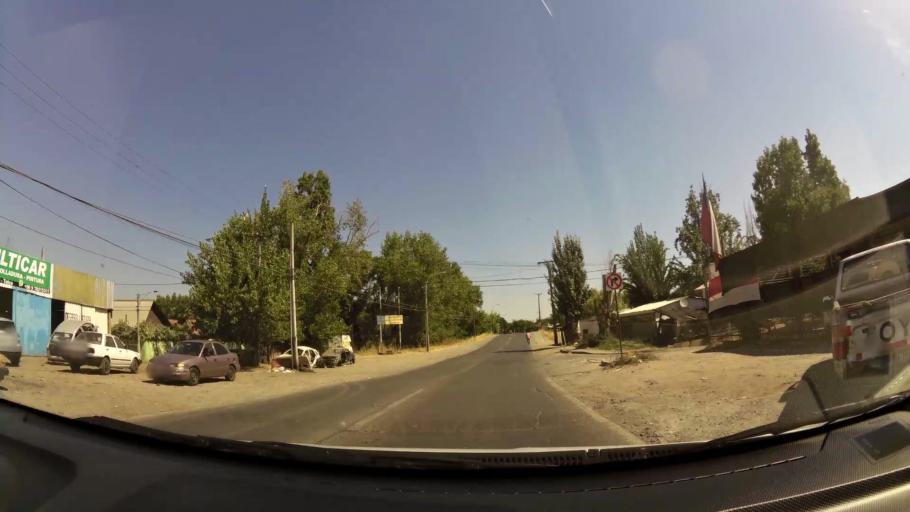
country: CL
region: Maule
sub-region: Provincia de Talca
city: Talca
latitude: -35.4389
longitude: -71.6516
